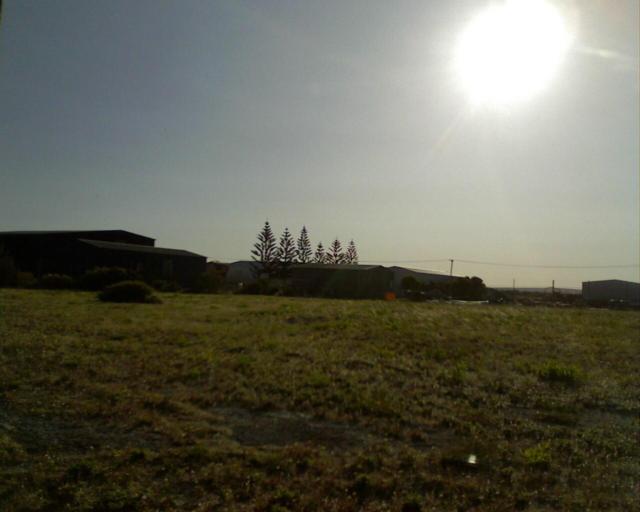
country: AU
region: Western Australia
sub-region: Dandaragan
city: Jurien Bay
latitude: -30.0533
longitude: 114.9773
